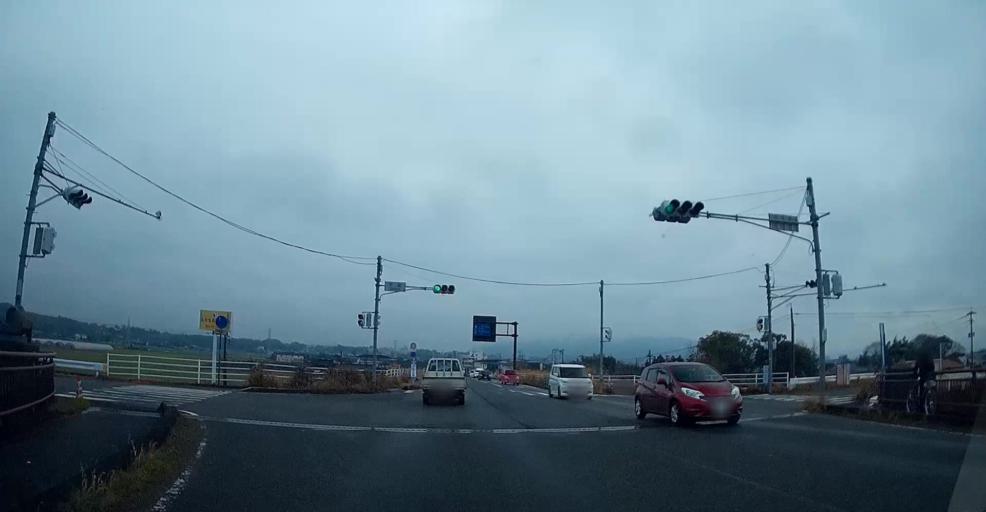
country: JP
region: Kumamoto
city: Kumamoto
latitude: 32.7336
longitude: 130.7389
